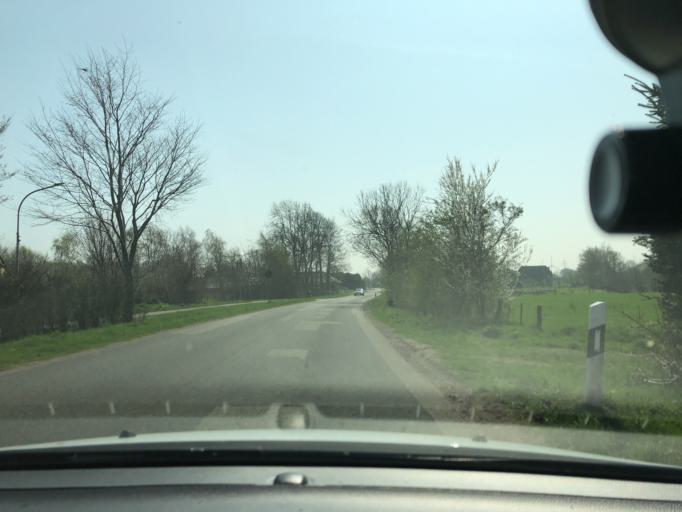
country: DE
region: Schleswig-Holstein
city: Grossenwiehe
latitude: 54.6905
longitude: 9.2401
